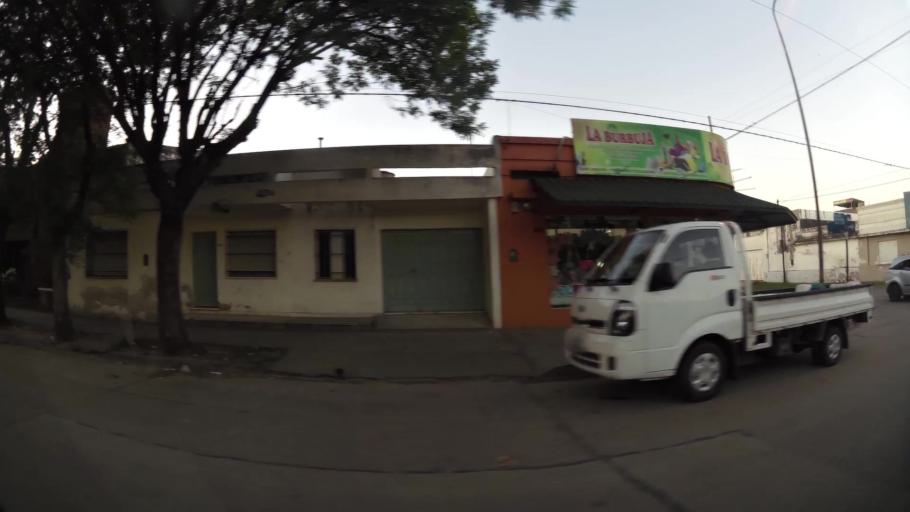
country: AR
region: Cordoba
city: Villa Maria
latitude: -32.4084
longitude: -63.2558
